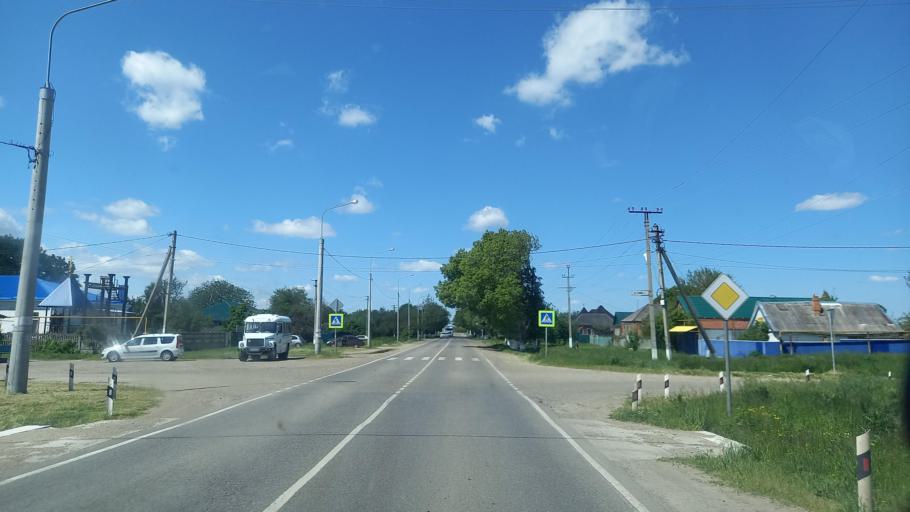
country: RU
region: Krasnodarskiy
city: Novoukrainskoye
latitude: 45.3805
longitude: 40.5060
